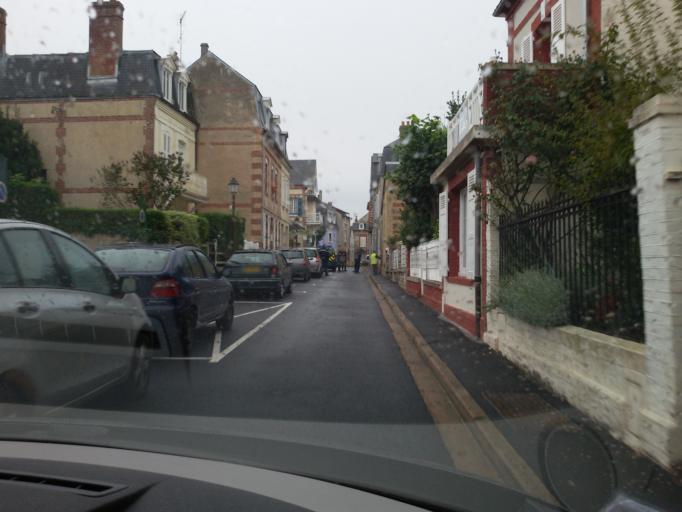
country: FR
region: Lower Normandy
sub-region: Departement du Calvados
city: Trouville-sur-Mer
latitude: 49.4010
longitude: 0.1286
